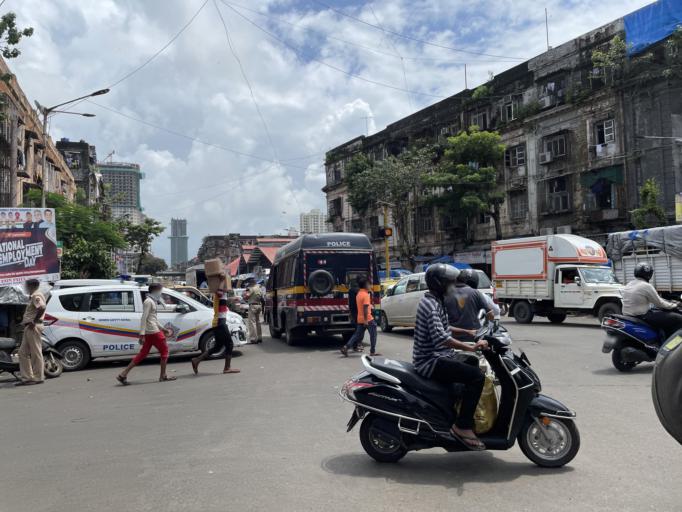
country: IN
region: Maharashtra
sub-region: Mumbai Suburban
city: Mumbai
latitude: 18.9582
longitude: 72.8285
